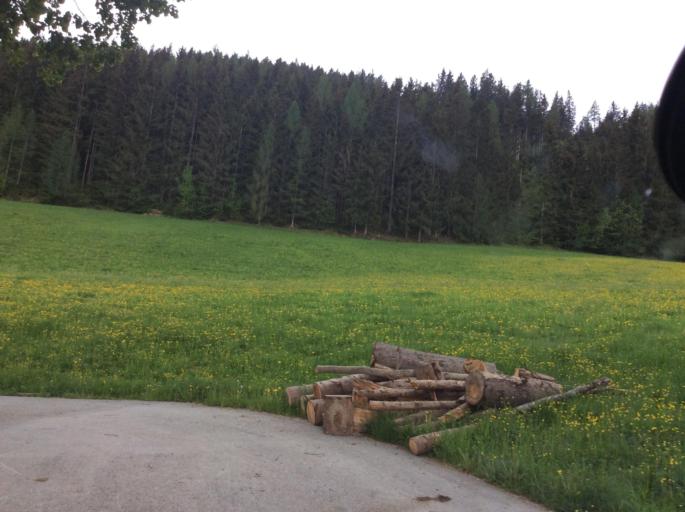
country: AT
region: Styria
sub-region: Politischer Bezirk Liezen
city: Schladming
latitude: 47.3859
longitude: 13.6511
